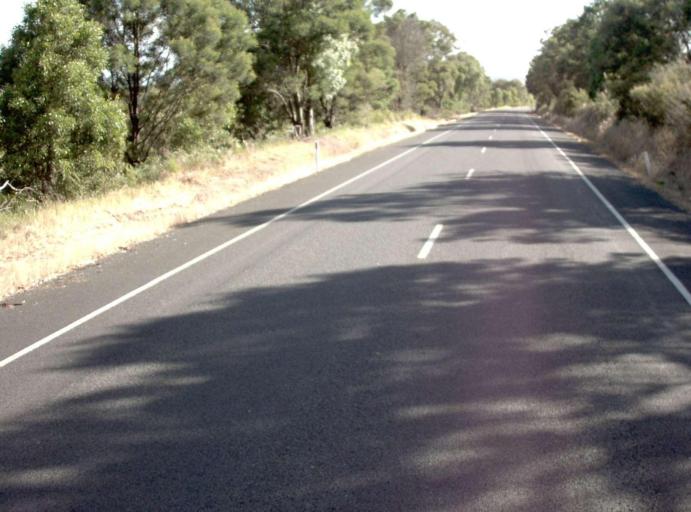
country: AU
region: Victoria
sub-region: East Gippsland
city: Lakes Entrance
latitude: -37.8506
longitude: 147.8472
